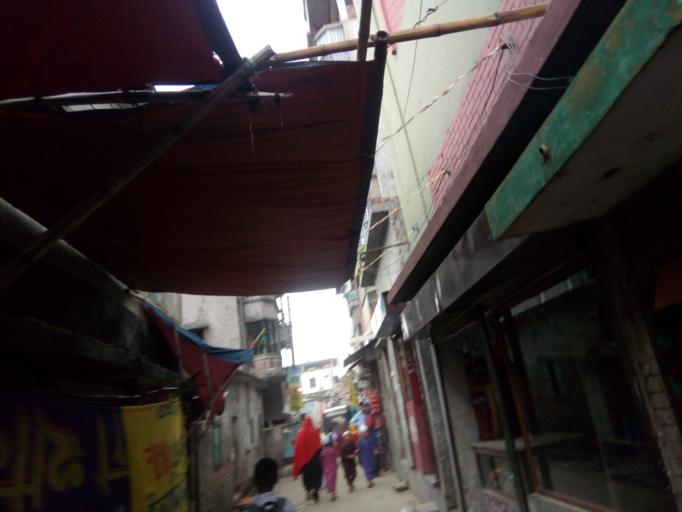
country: BD
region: Dhaka
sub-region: Dhaka
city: Dhaka
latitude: 23.6851
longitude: 90.4462
